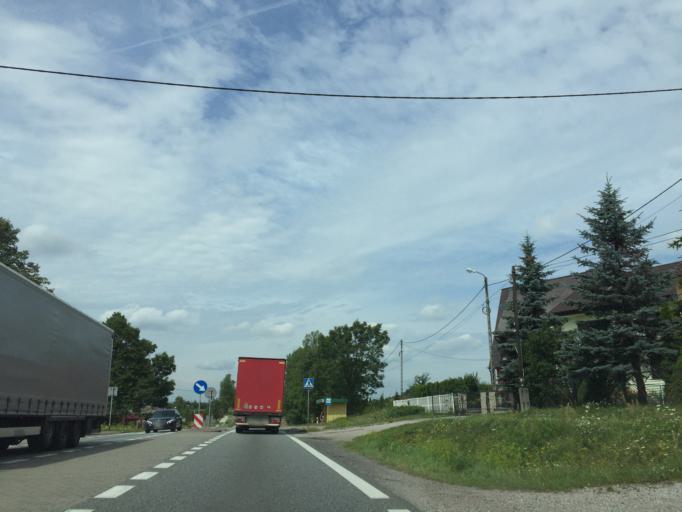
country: PL
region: Lesser Poland Voivodeship
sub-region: Powiat krakowski
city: Przeginia
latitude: 50.2510
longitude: 19.6592
